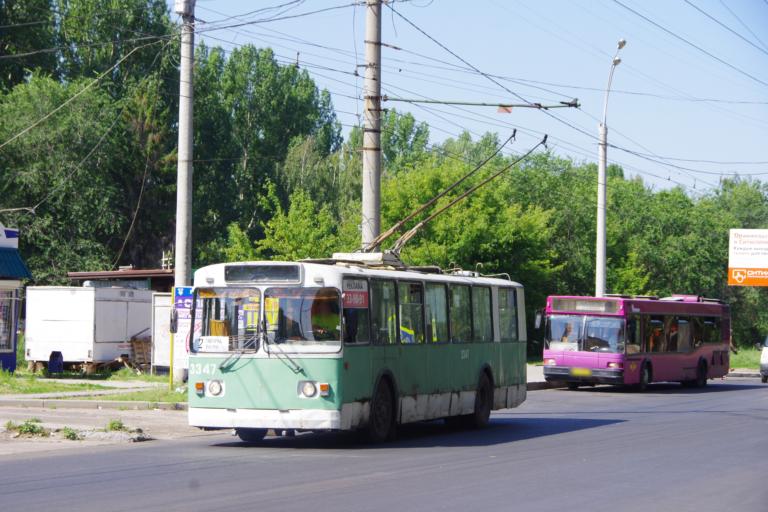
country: RU
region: Samara
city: Tol'yatti
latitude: 53.5098
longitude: 49.4285
